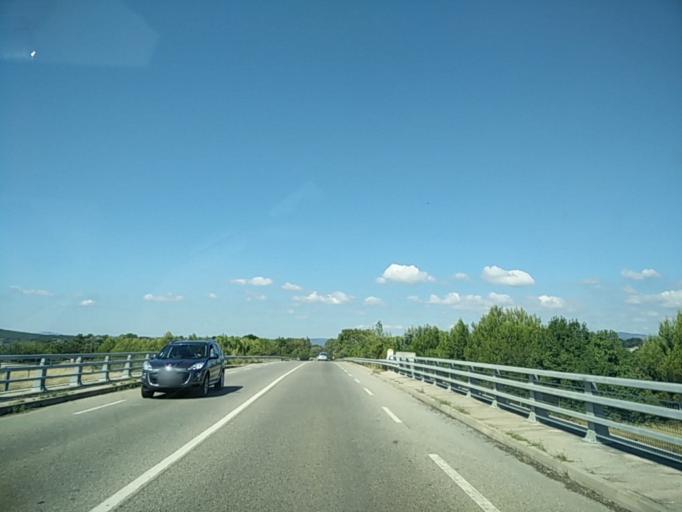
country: FR
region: Rhone-Alpes
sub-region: Departement de la Drome
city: Montboucher-sur-Jabron
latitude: 44.5478
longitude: 4.8250
